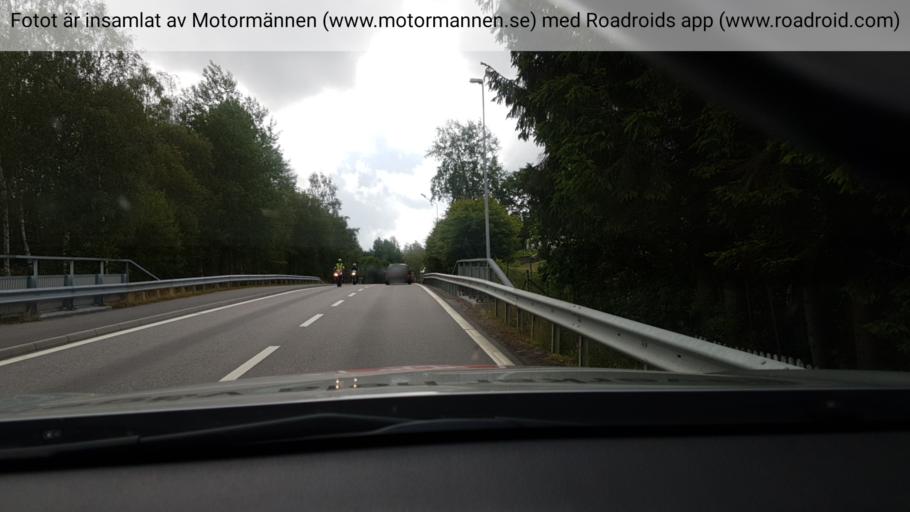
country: SE
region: Vaestra Goetaland
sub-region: Svenljunga Kommun
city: Svenljunga
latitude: 57.4937
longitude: 13.1238
